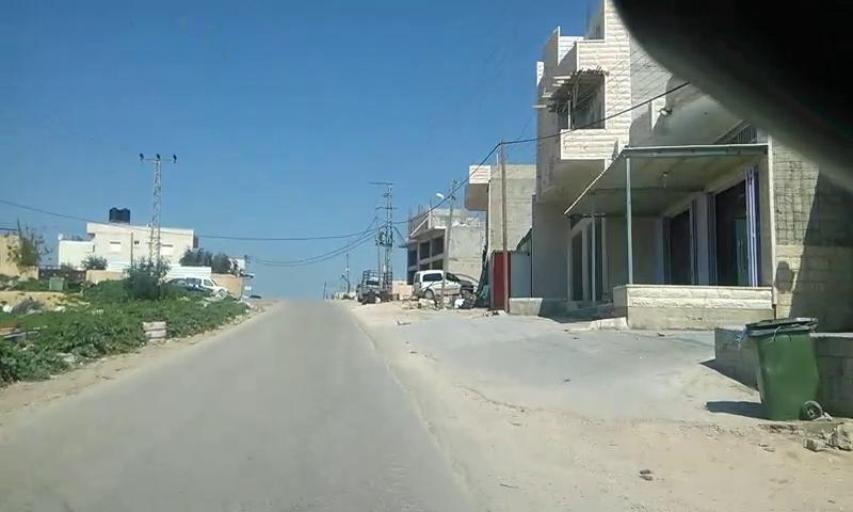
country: PS
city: Dayr Samit
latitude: 31.5044
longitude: 34.9677
